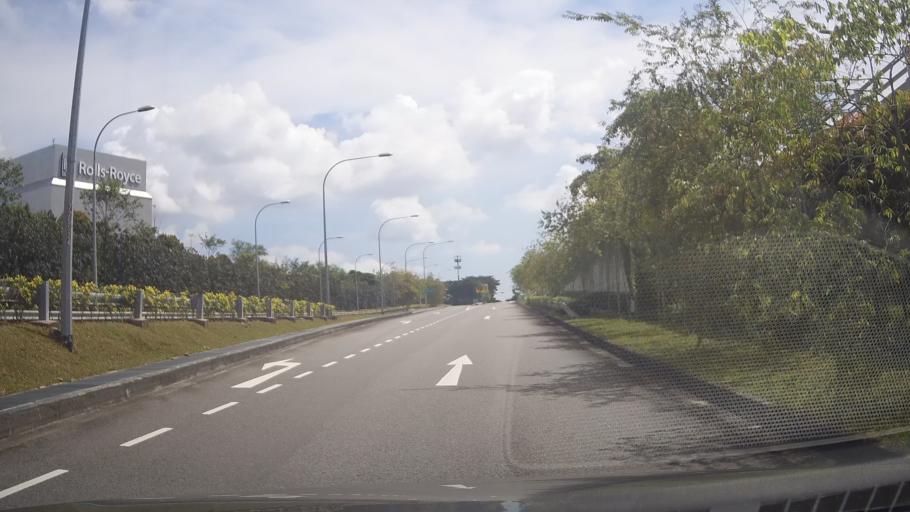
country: MY
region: Johor
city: Kampung Pasir Gudang Baru
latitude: 1.4015
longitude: 103.8661
